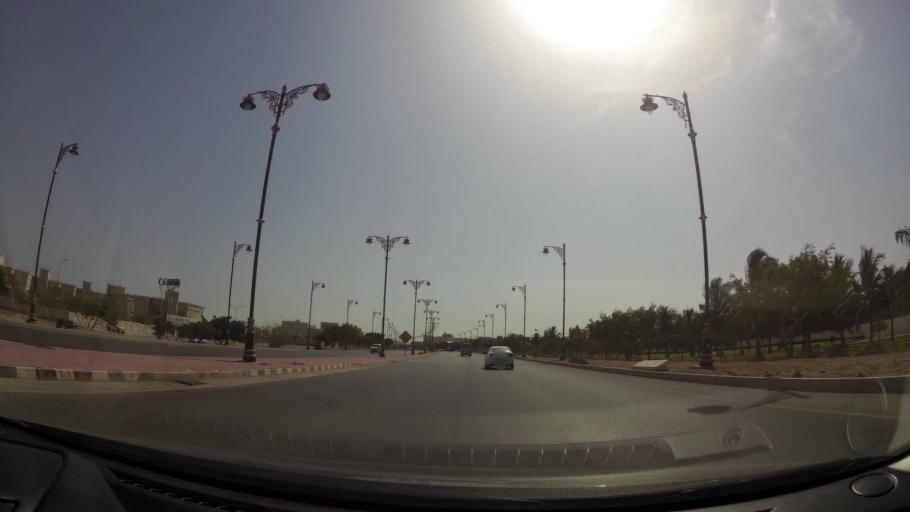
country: OM
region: Zufar
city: Salalah
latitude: 17.0233
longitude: 54.0730
